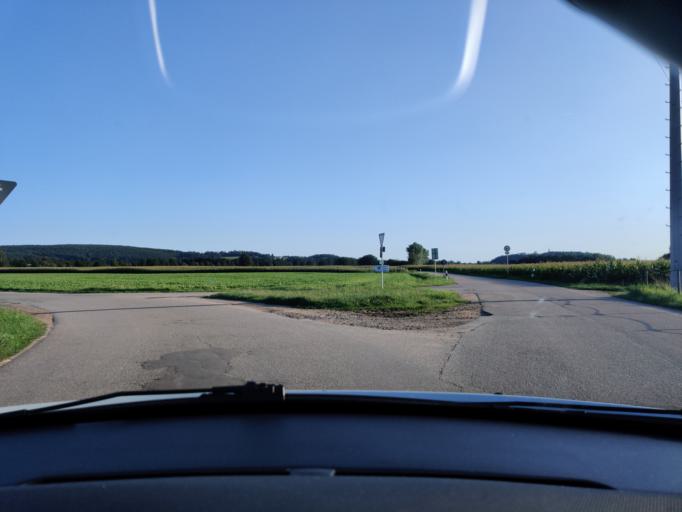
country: DE
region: Bavaria
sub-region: Upper Palatinate
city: Stulln
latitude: 49.4098
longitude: 12.1594
